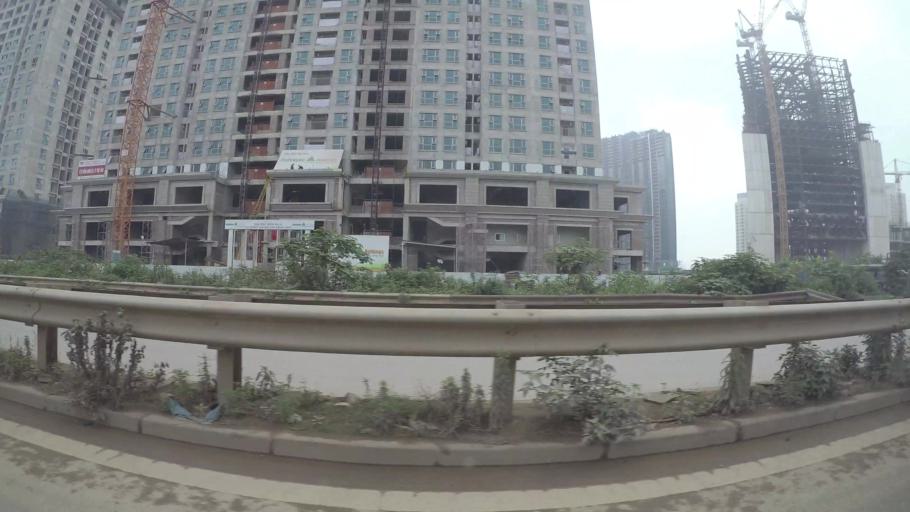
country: VN
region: Ha Noi
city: Tay Ho
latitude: 21.0843
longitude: 105.7880
